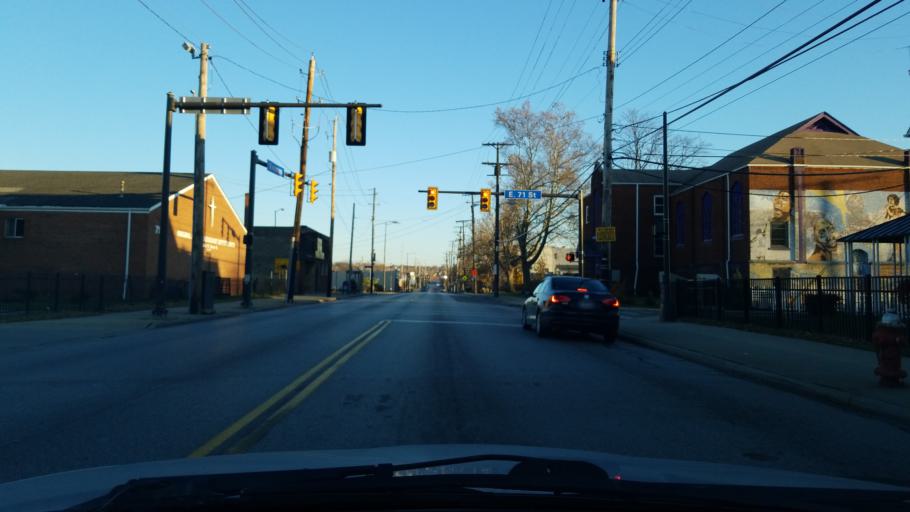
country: US
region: Ohio
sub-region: Cuyahoga County
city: Newburgh Heights
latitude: 41.4802
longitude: -81.6394
